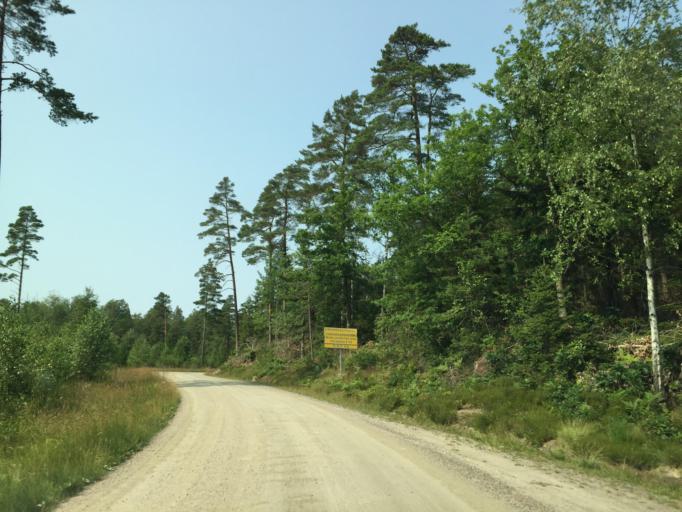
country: SE
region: Vaestra Goetaland
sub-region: Lilla Edets Kommun
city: Lilla Edet
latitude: 58.2323
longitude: 12.1123
